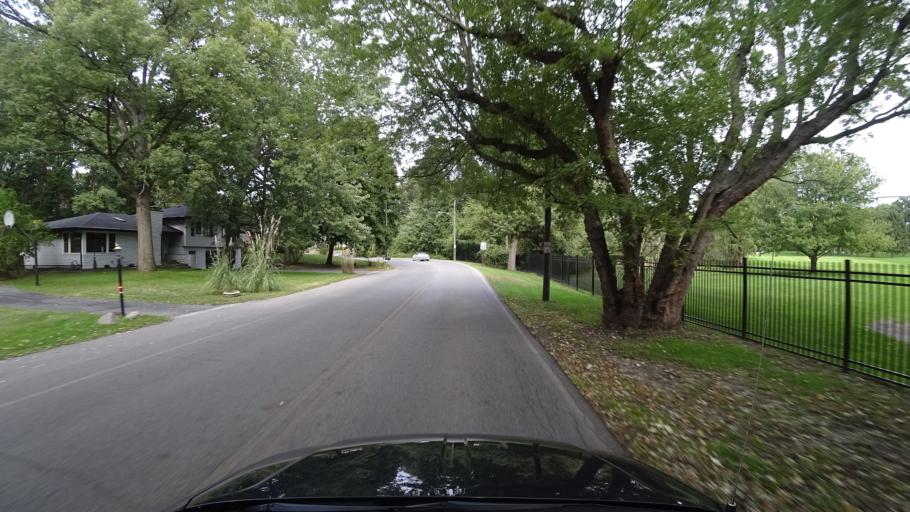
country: US
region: Indiana
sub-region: LaPorte County
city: Long Beach
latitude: 41.7402
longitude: -86.8550
